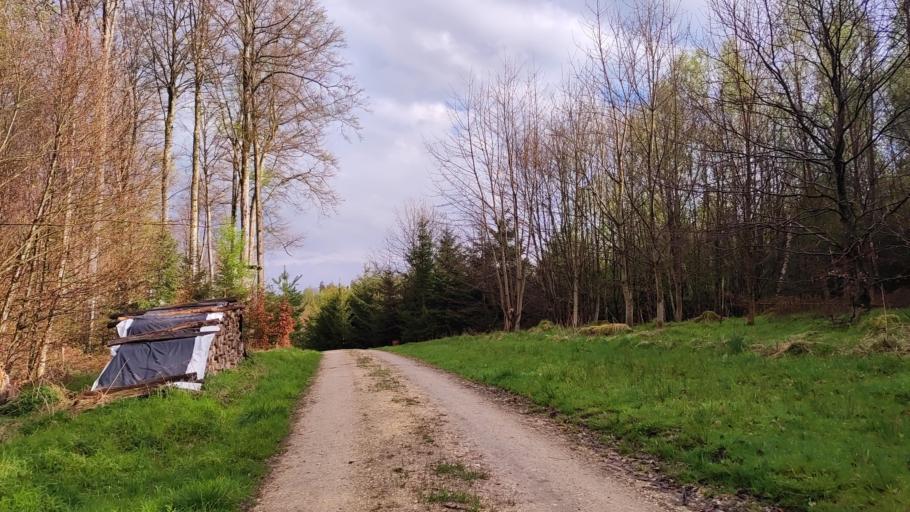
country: DE
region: Bavaria
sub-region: Swabia
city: Zusmarshausen
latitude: 48.4202
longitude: 10.6179
